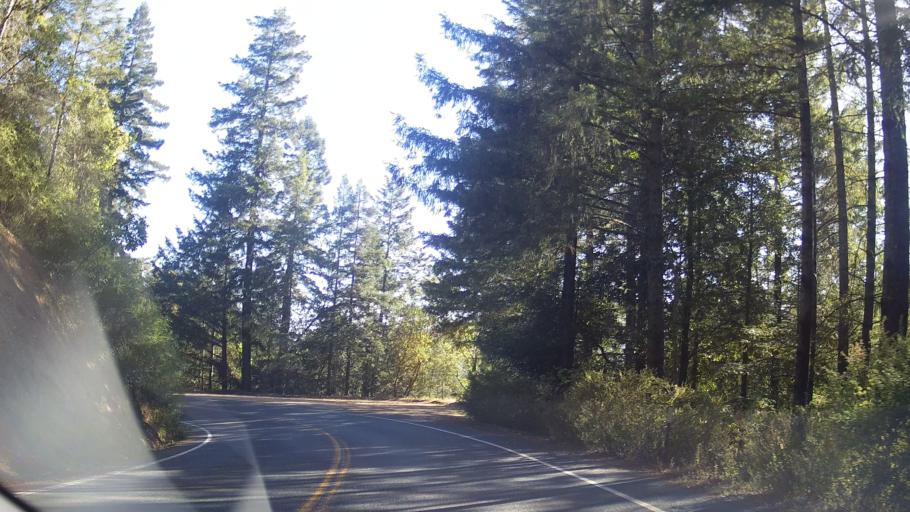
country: US
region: California
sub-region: Mendocino County
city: Brooktrails
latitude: 39.3700
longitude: -123.4971
